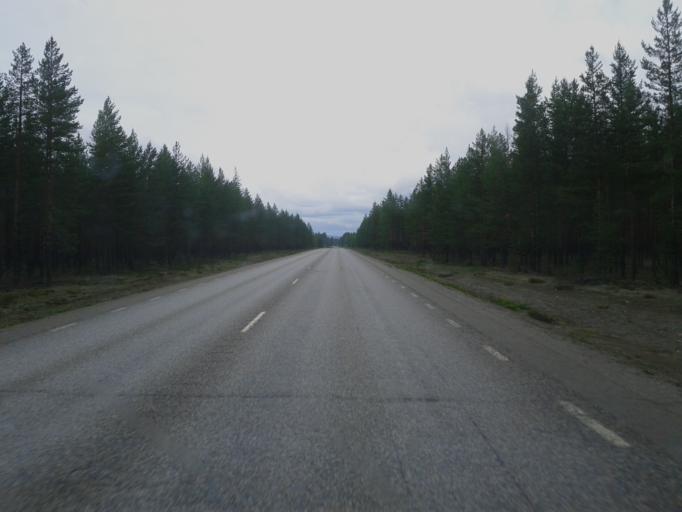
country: SE
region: Vaesterbotten
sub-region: Skelleftea Kommun
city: Langsele
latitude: 64.9497
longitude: 19.9100
